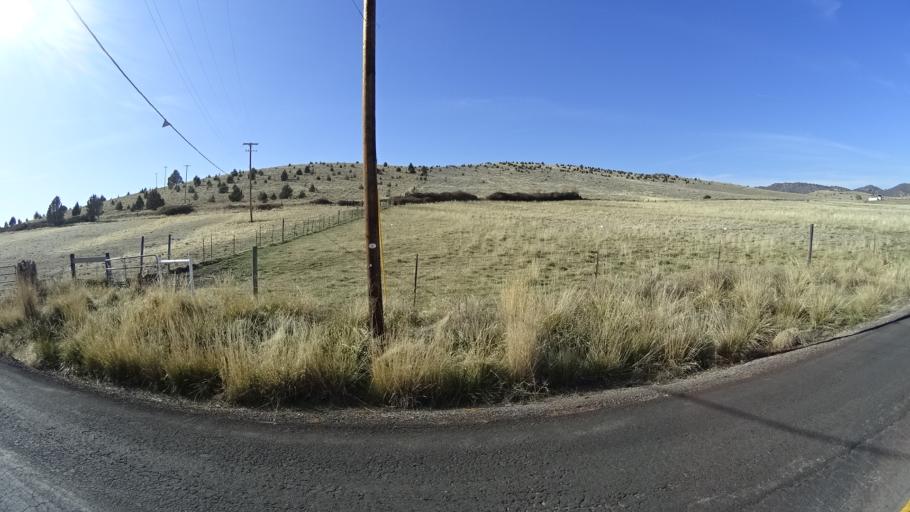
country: US
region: California
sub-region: Siskiyou County
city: Montague
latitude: 41.6037
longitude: -122.5305
